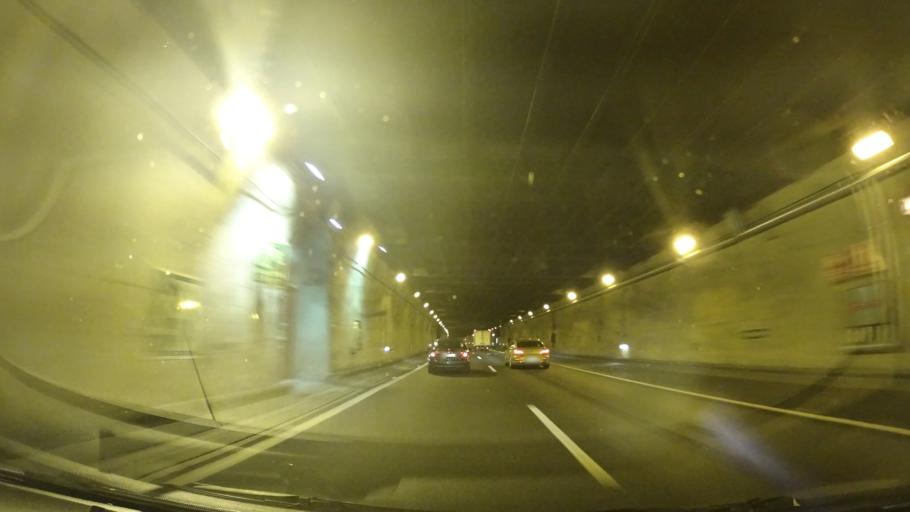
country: ES
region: Madrid
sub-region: Provincia de Madrid
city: Guadarrama
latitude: 40.7123
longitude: -4.1433
